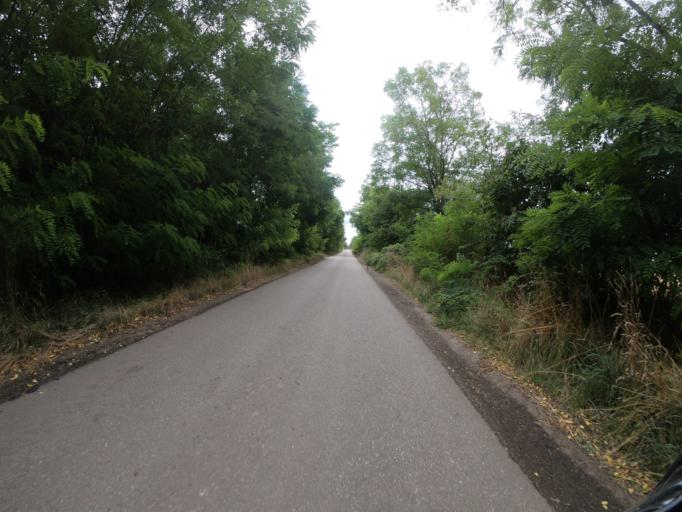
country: HU
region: Borsod-Abauj-Zemplen
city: Szentistvan
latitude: 47.7123
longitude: 20.6943
